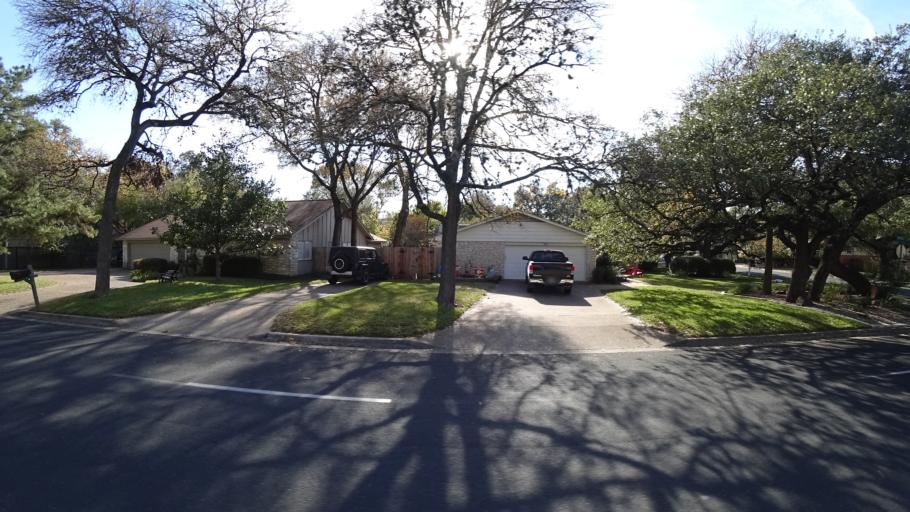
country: US
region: Texas
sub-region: Williamson County
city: Jollyville
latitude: 30.3807
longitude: -97.7515
